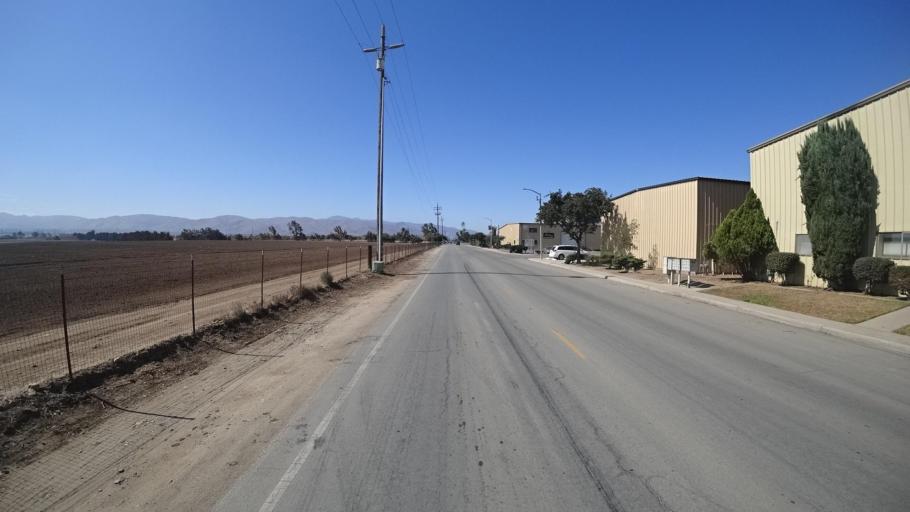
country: US
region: California
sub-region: Monterey County
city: Greenfield
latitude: 36.3220
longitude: -121.2332
